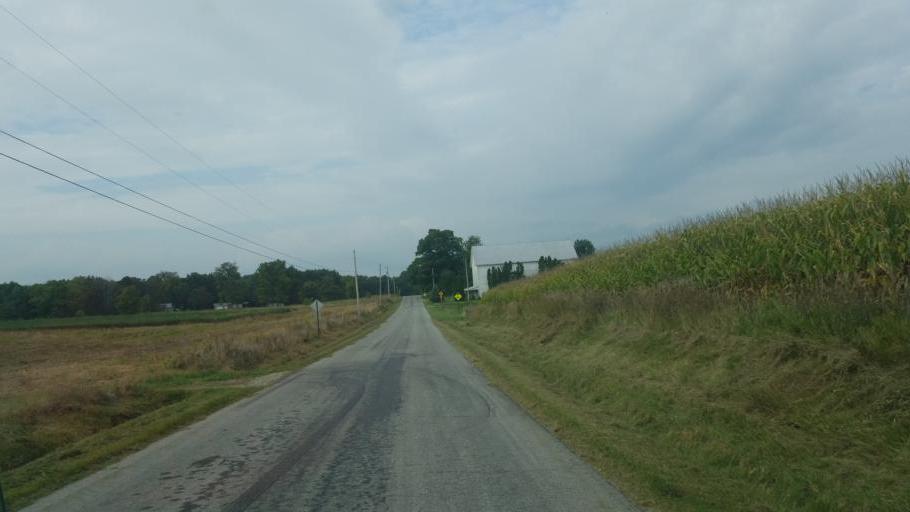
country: US
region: Ohio
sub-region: Wayne County
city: West Salem
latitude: 40.9417
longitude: -82.0578
